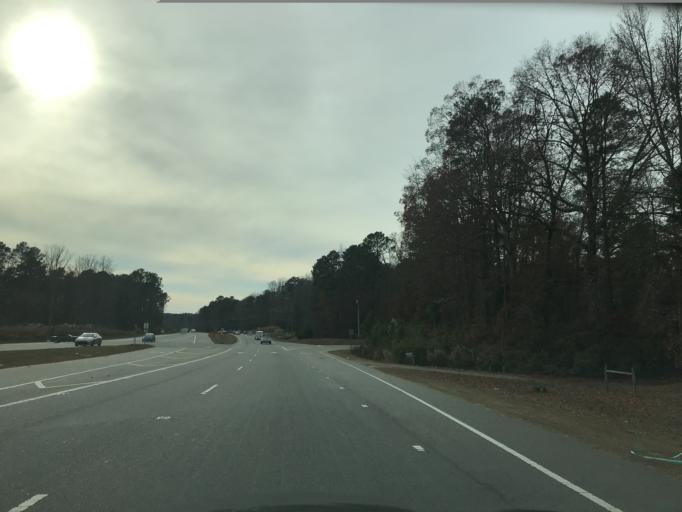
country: US
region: North Carolina
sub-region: Wake County
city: Rolesville
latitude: 35.8912
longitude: -78.5191
